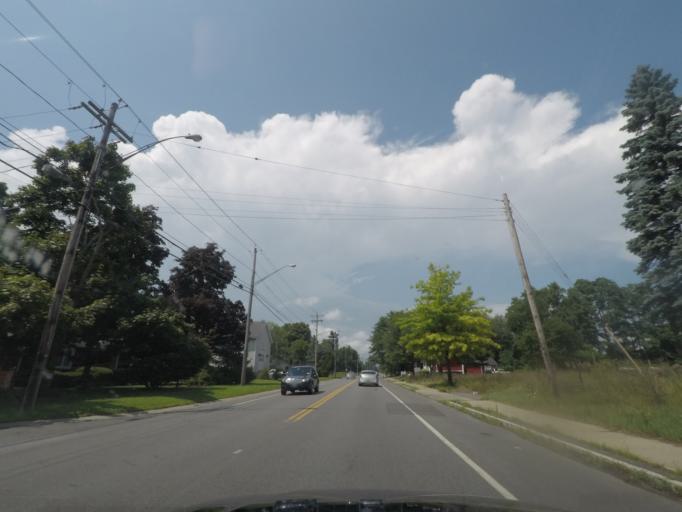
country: US
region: New York
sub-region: Albany County
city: West Albany
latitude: 42.7117
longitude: -73.7816
